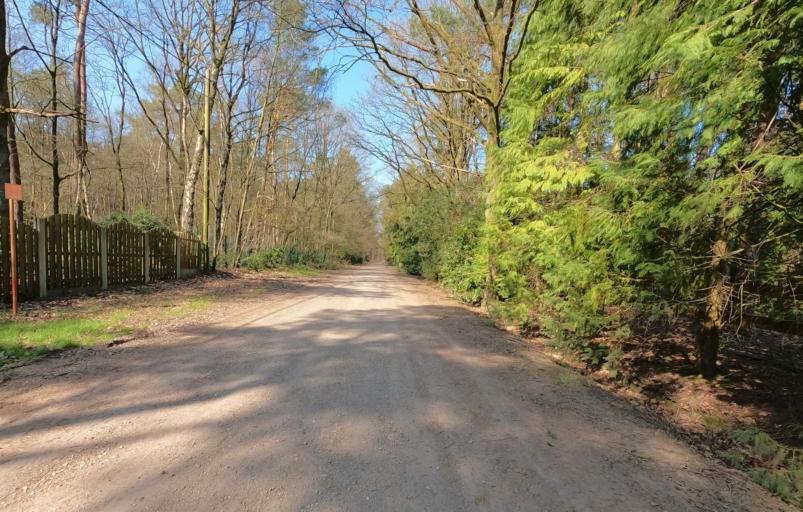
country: BE
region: Flanders
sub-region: Provincie Antwerpen
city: Schilde
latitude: 51.2855
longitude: 4.6184
